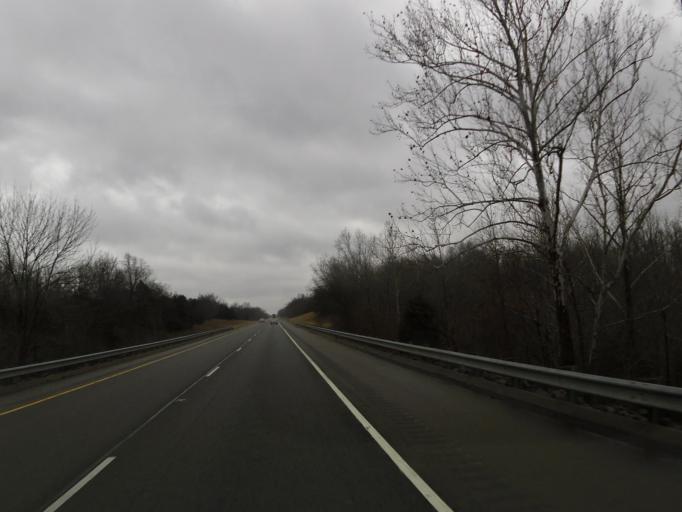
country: US
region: Illinois
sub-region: Johnson County
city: Vienna
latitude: 37.3690
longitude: -88.8070
